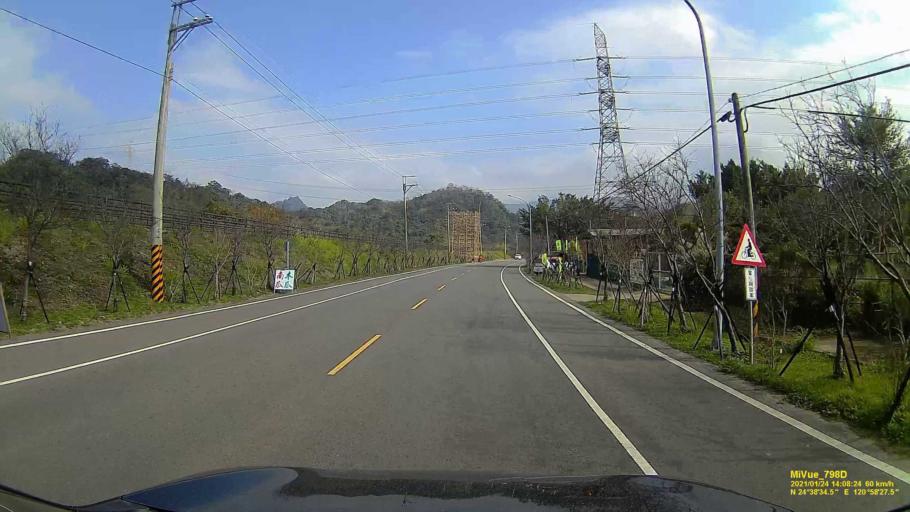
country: TW
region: Taiwan
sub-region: Hsinchu
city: Hsinchu
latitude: 24.6430
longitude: 120.9751
